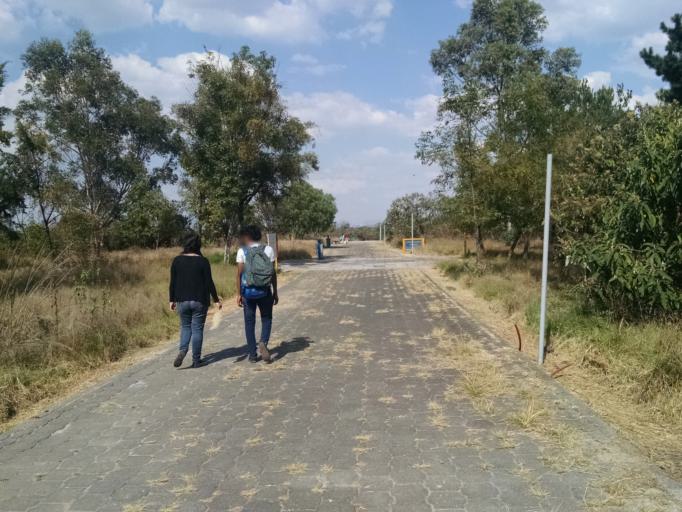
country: MX
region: Mexico City
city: Tlalpan
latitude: 19.3176
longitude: -99.1836
